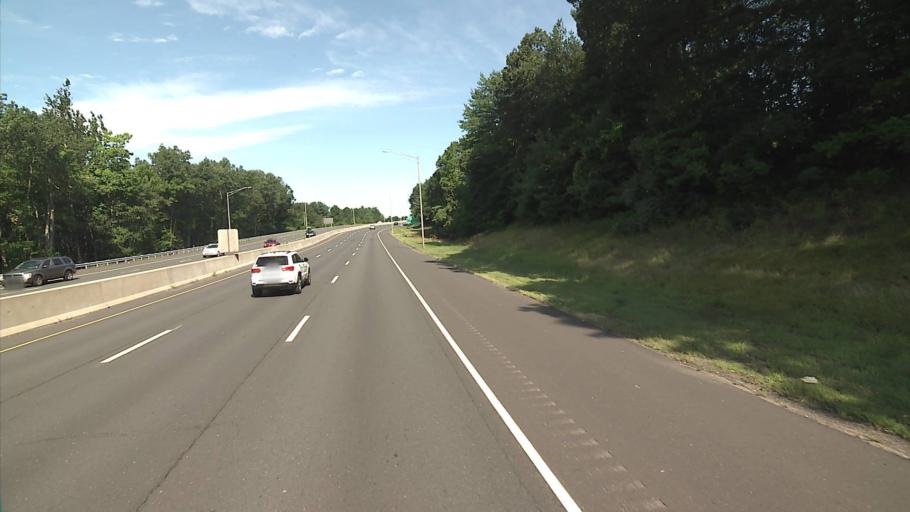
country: US
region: Connecticut
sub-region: Hartford County
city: Glastonbury
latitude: 41.7197
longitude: -72.6037
